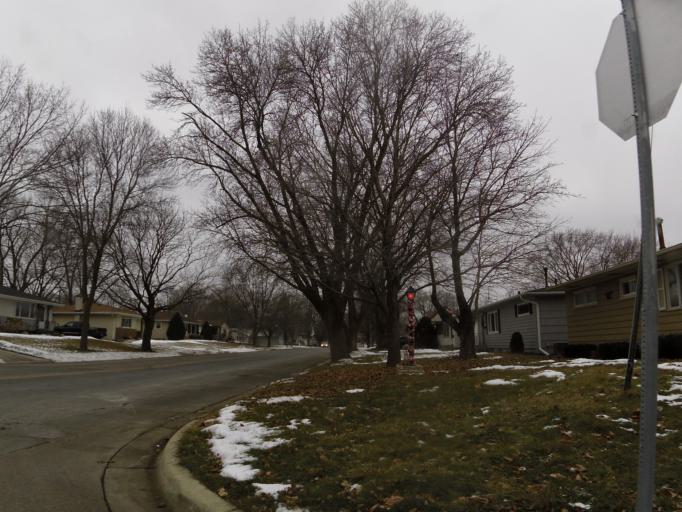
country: US
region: Minnesota
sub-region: Carver County
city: Waconia
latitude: 44.8473
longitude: -93.7893
